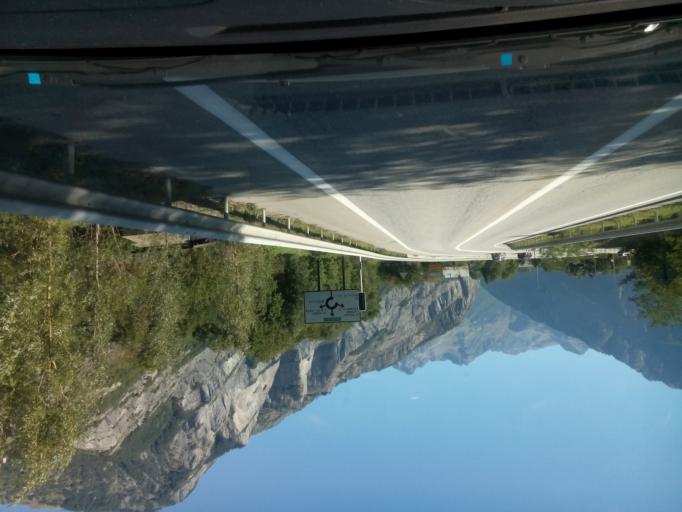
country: FR
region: Rhone-Alpes
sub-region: Departement de l'Isere
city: Huez
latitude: 45.0582
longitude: 6.0394
